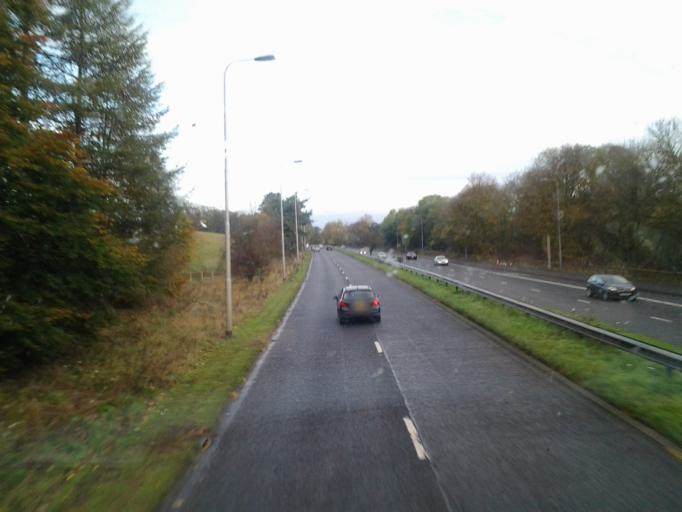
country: GB
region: England
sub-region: County Durham
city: Durham
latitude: 54.8103
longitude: -1.5887
